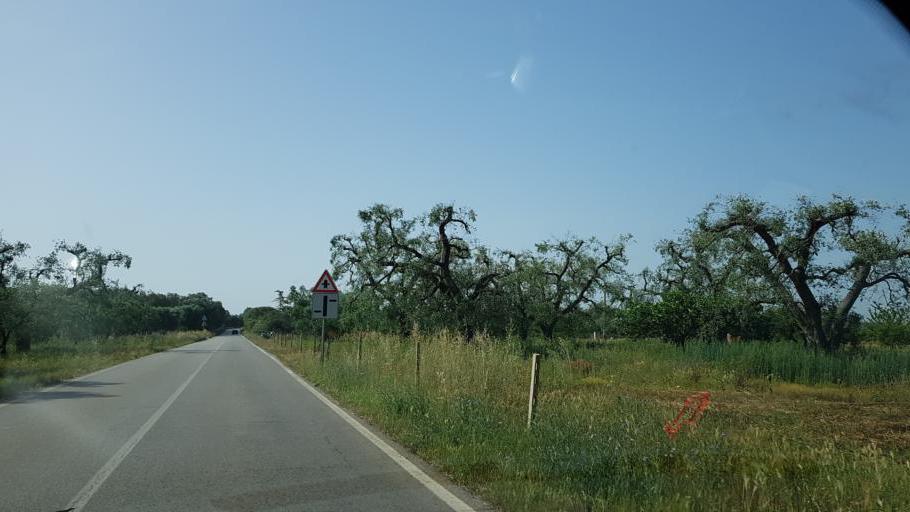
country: IT
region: Apulia
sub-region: Provincia di Brindisi
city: Mesagne
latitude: 40.5200
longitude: 17.8231
